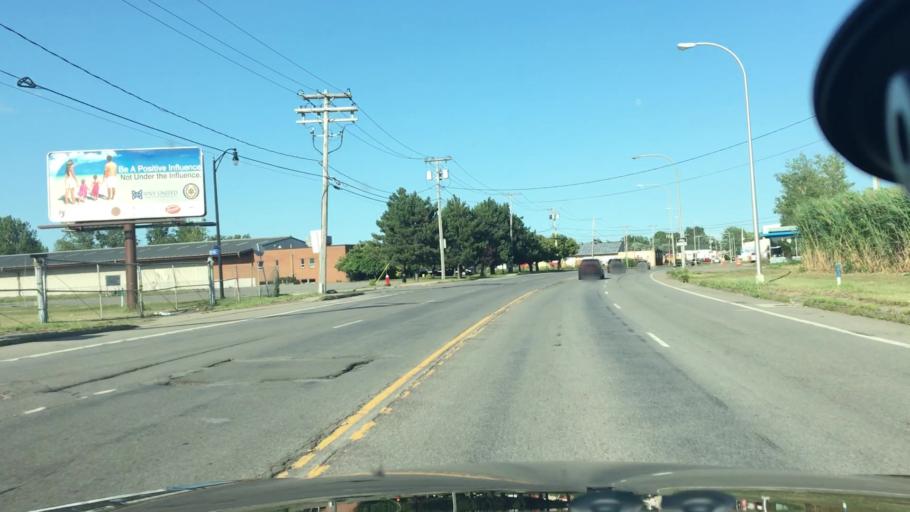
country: US
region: New York
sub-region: Erie County
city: Lackawanna
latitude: 42.8469
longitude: -78.8378
